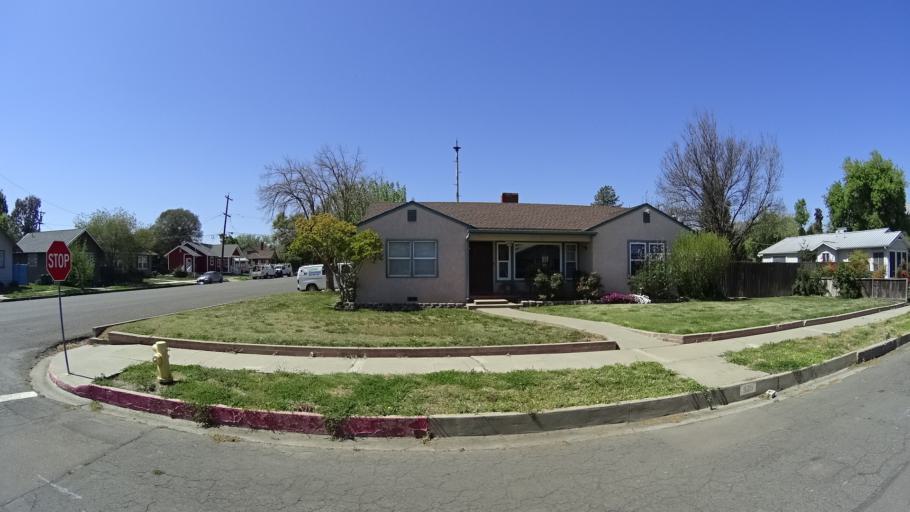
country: US
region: California
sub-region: Glenn County
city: Willows
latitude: 39.5143
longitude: -122.1967
